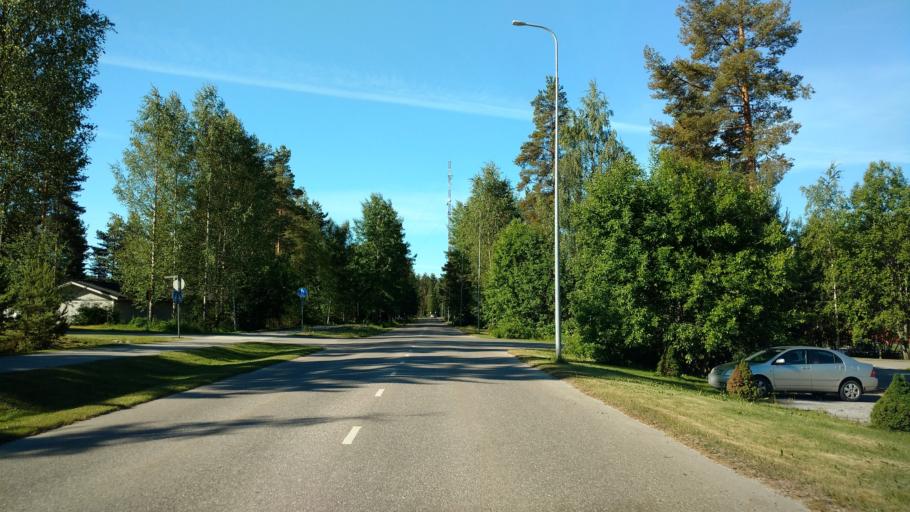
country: FI
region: Varsinais-Suomi
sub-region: Salo
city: Salo
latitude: 60.3926
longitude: 23.1862
